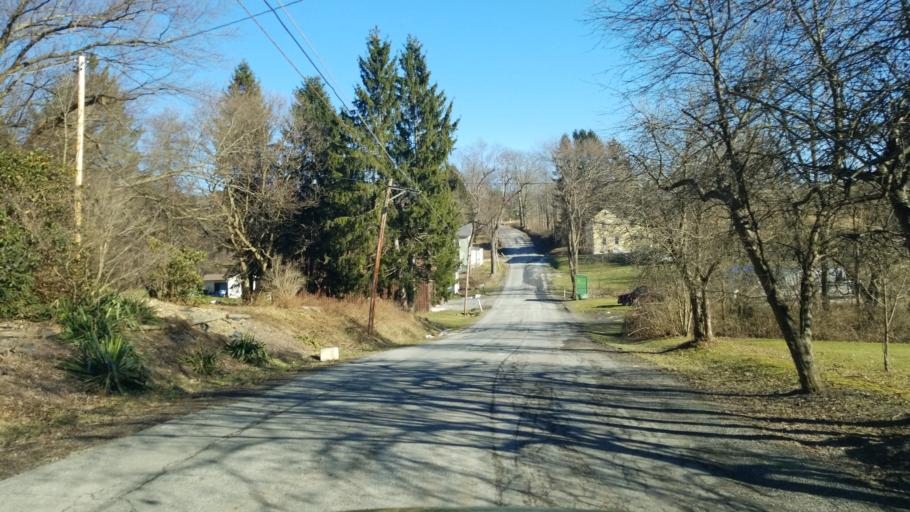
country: US
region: Pennsylvania
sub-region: Jefferson County
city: Sykesville
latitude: 41.0482
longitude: -78.7636
